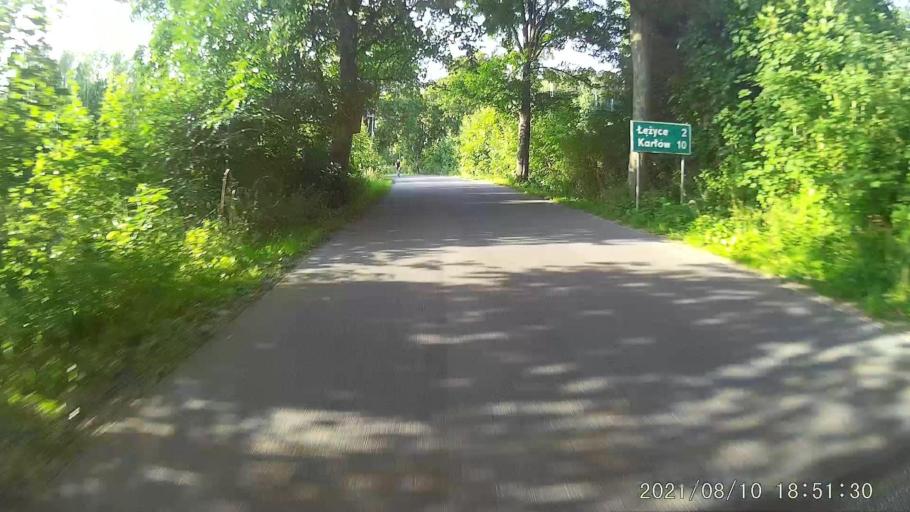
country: PL
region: Lower Silesian Voivodeship
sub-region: Powiat klodzki
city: Duszniki-Zdroj
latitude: 50.4118
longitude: 16.3808
